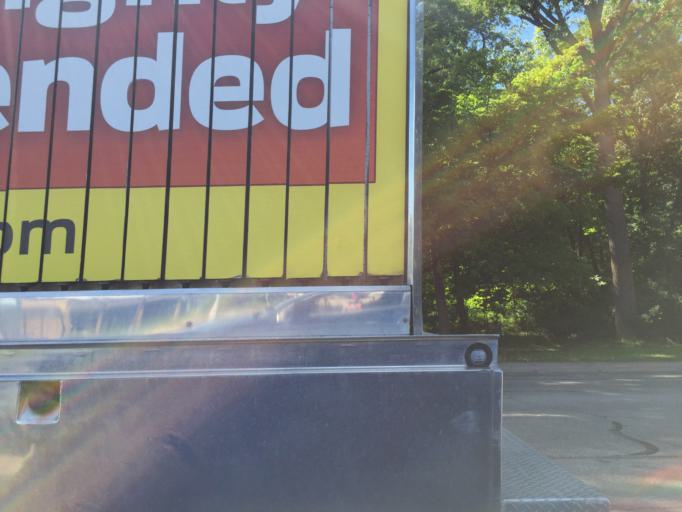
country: US
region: Michigan
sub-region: Wayne County
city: Highland Park
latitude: 42.4252
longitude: -83.1106
